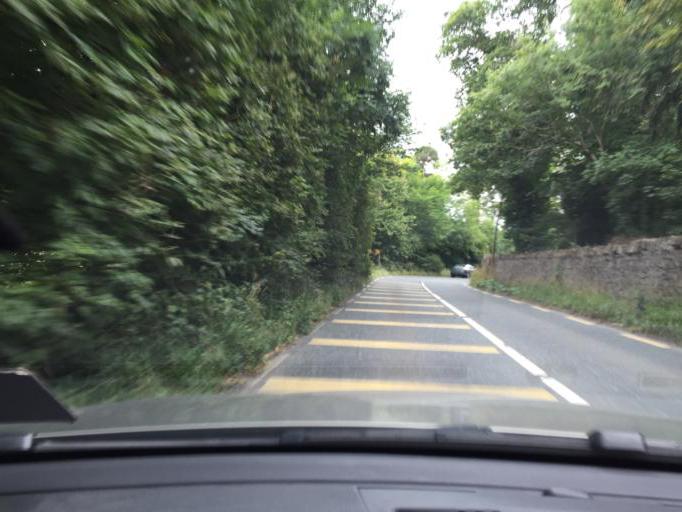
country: IE
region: Leinster
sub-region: Kildare
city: Maynooth
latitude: 53.3986
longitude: -6.5595
